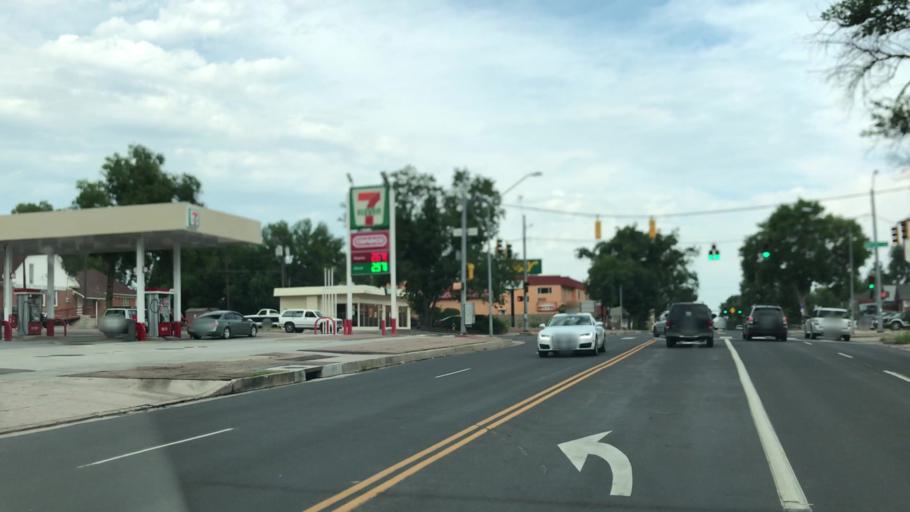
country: US
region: Colorado
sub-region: El Paso County
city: Manitou Springs
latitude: 38.8521
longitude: -104.8707
